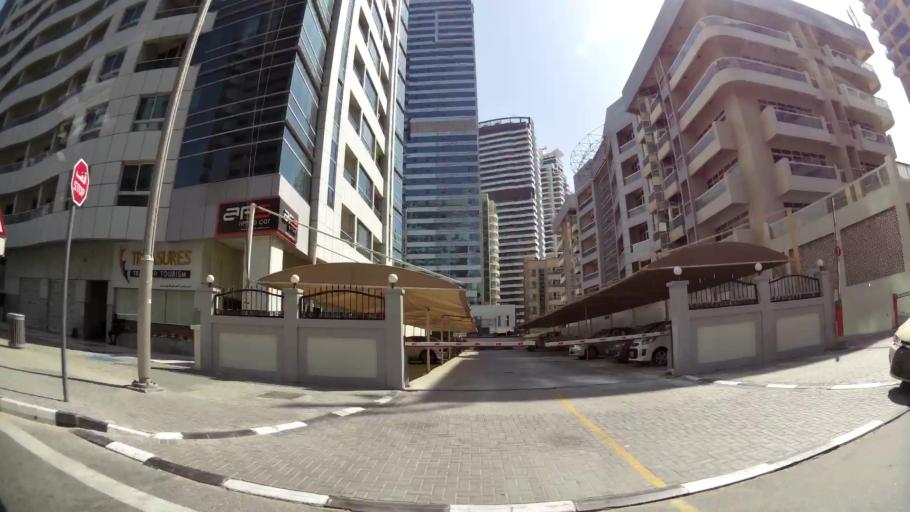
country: AE
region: Dubai
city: Dubai
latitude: 25.0698
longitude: 55.1347
